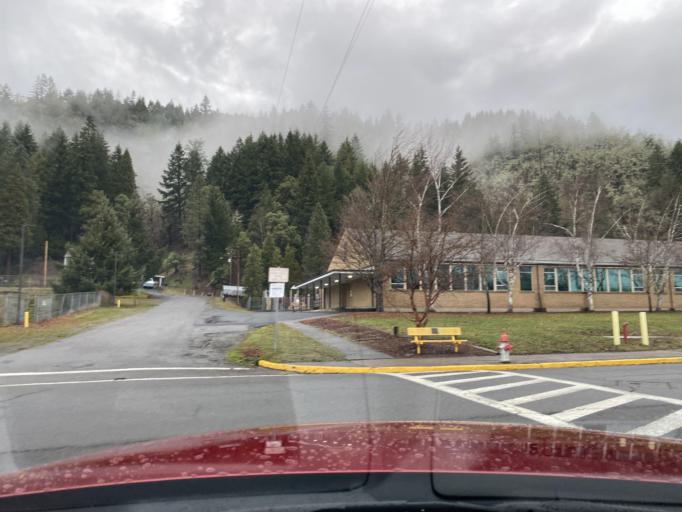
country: US
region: Oregon
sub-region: Lane County
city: Oakridge
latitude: 43.7480
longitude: -122.4661
